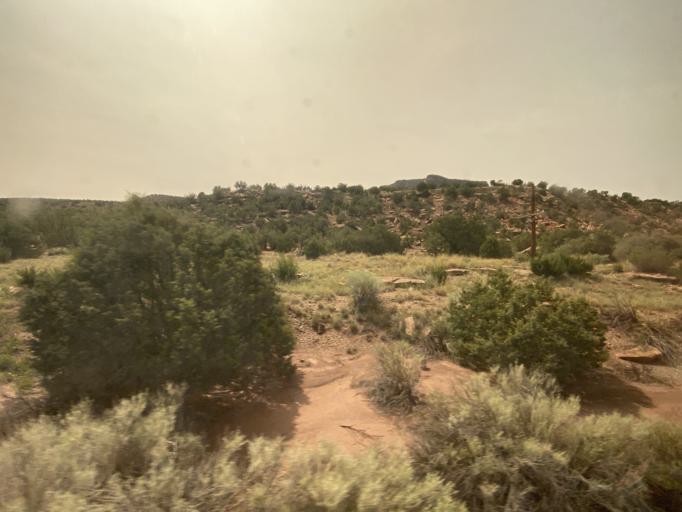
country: US
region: New Mexico
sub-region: San Miguel County
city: Pecos
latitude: 35.3974
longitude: -105.4928
